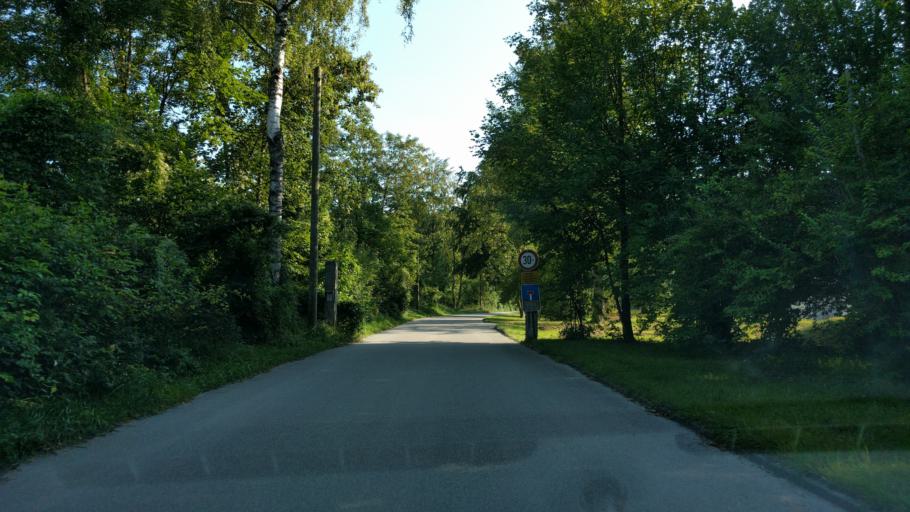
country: DE
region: Bavaria
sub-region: Upper Bavaria
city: Grunwald
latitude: 48.0330
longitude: 11.5075
